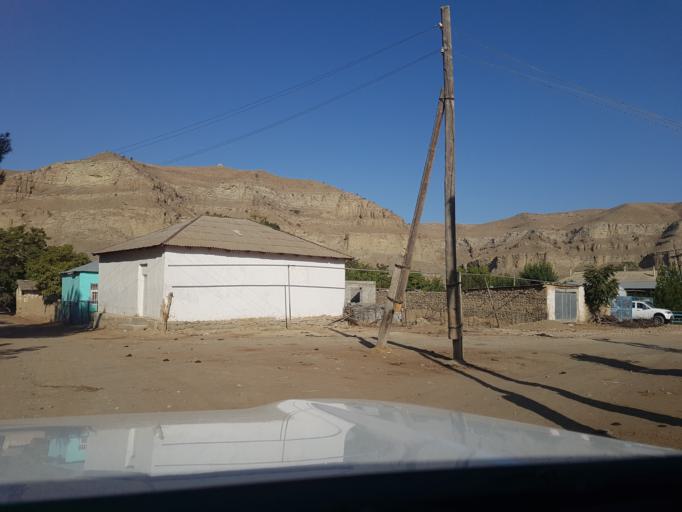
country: TM
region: Balkan
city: Magtymguly
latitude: 38.3011
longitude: 56.7445
